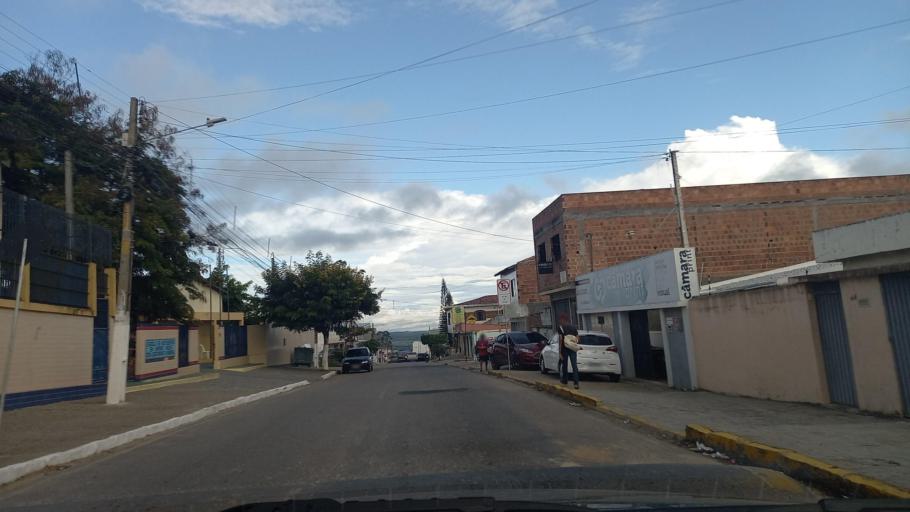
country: BR
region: Pernambuco
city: Garanhuns
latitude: -8.9022
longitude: -36.4925
